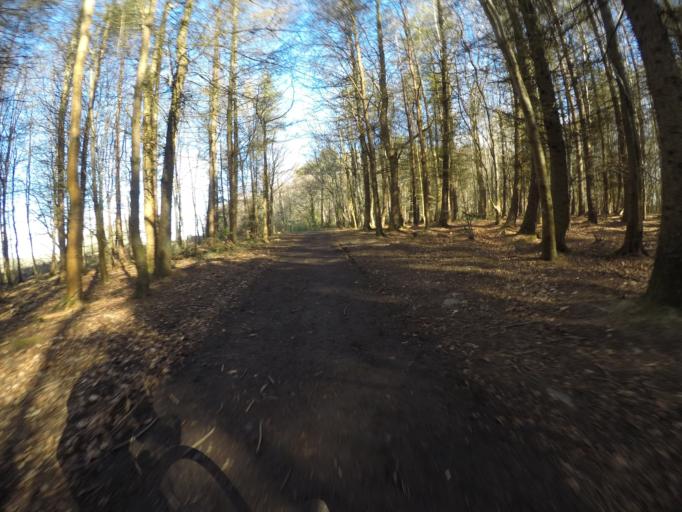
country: GB
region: Scotland
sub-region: North Ayrshire
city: Irvine
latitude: 55.6396
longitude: -4.6566
